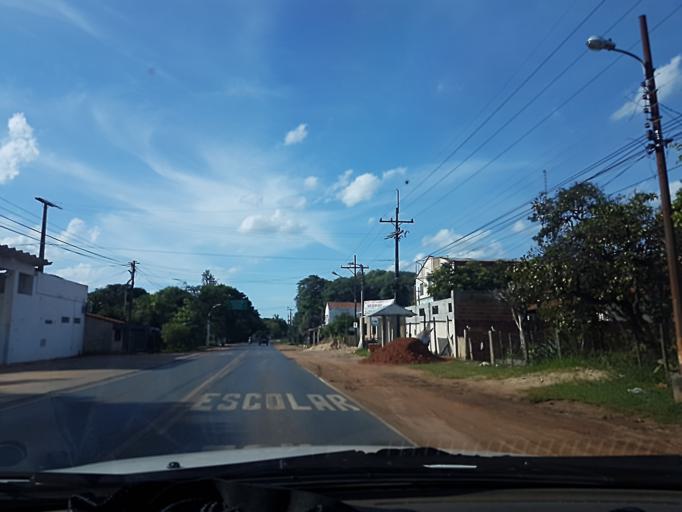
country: PY
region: Central
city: Limpio
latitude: -25.1904
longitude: -57.4639
